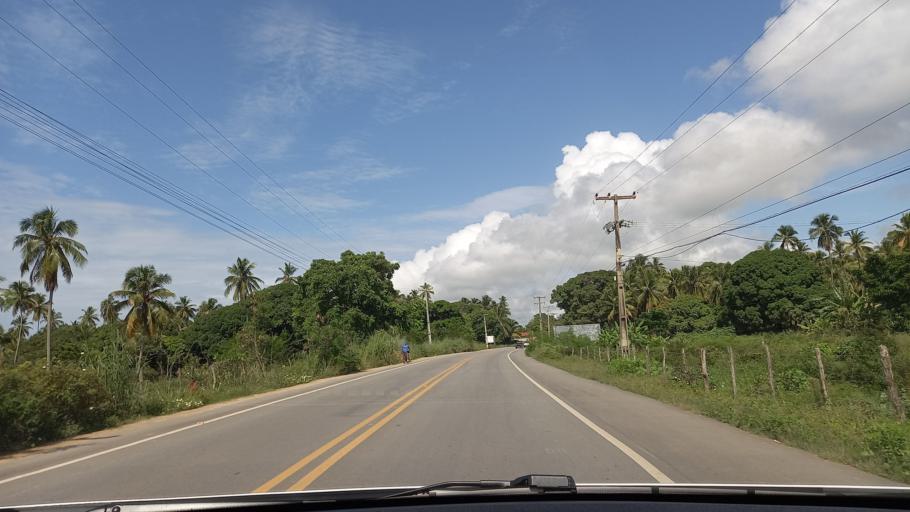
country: BR
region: Alagoas
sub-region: Maragogi
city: Maragogi
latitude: -8.9895
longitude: -35.2016
